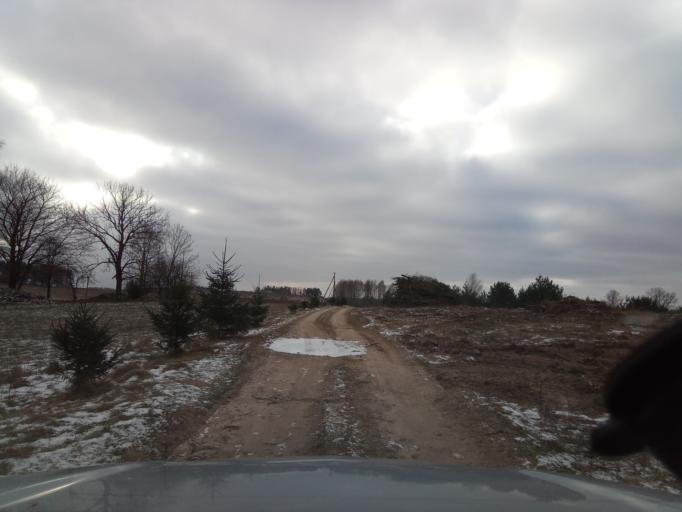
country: LT
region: Alytaus apskritis
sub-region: Alytaus rajonas
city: Daugai
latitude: 54.3310
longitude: 24.2909
